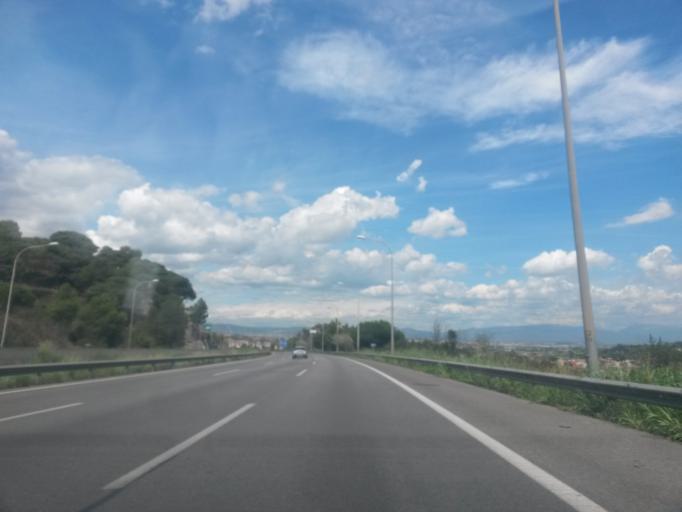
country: ES
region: Catalonia
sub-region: Provincia de Barcelona
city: Montcada i Reixac
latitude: 41.4793
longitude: 2.1847
